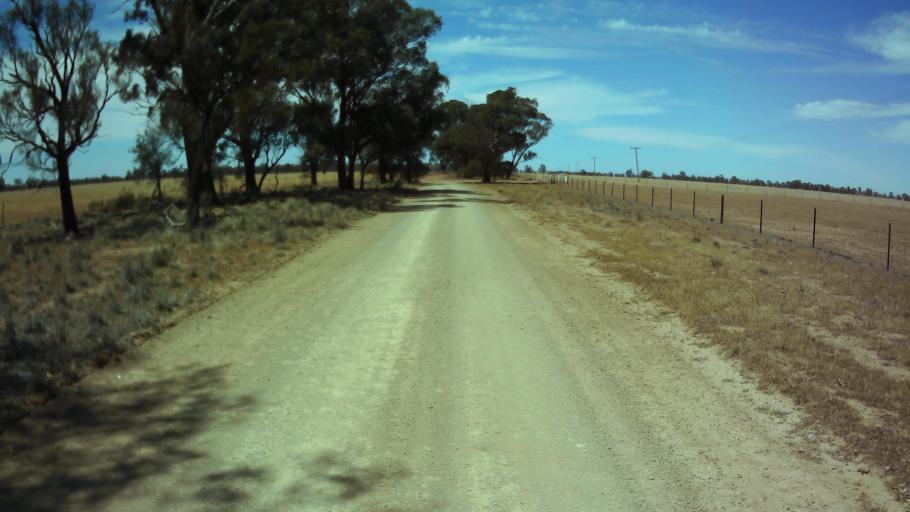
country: AU
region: New South Wales
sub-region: Weddin
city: Grenfell
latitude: -33.8903
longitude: 147.8034
